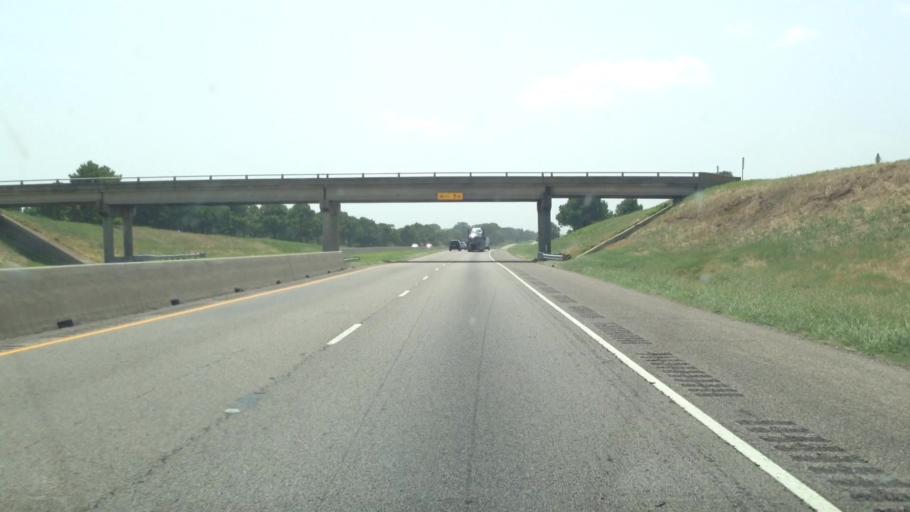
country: US
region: Texas
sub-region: Hopkins County
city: Sulphur Springs
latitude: 33.1472
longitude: -95.4565
